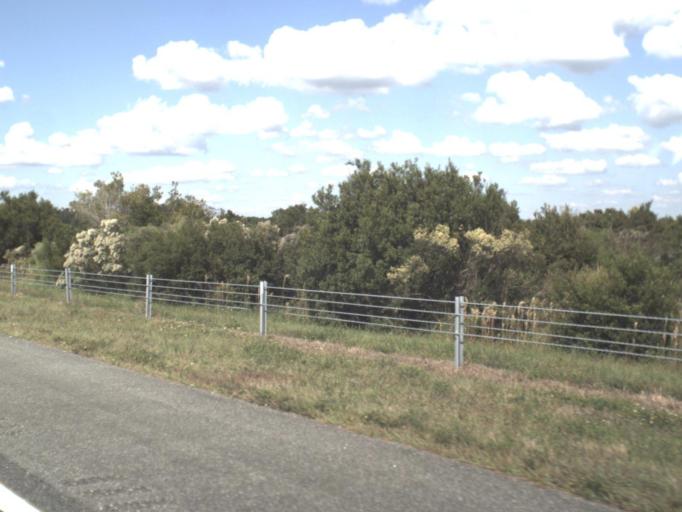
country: US
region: Florida
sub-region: Indian River County
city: Fellsmere
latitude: 27.8011
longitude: -80.9938
